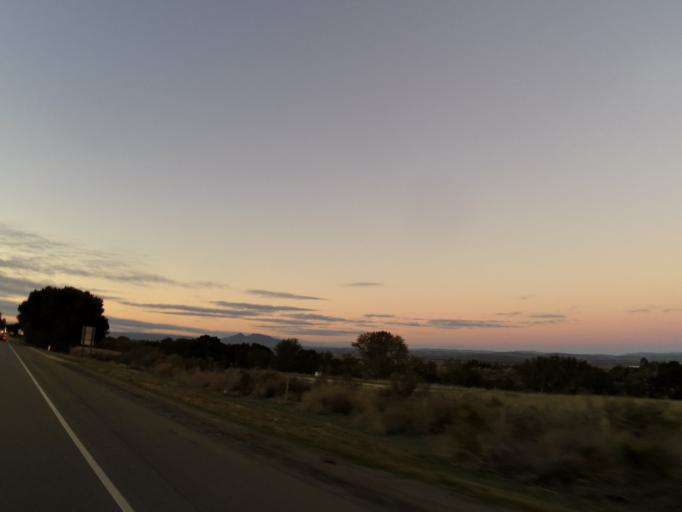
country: US
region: California
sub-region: Monterey County
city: King City
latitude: 36.2015
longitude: -121.1548
